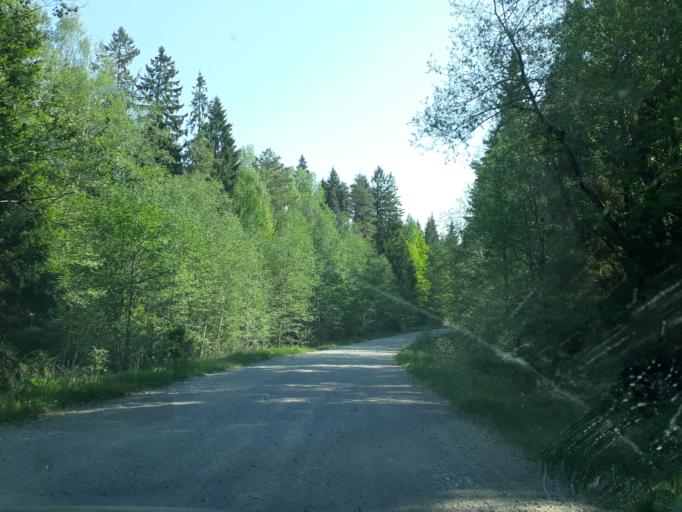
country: LV
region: Ligatne
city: Ligatne
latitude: 57.2799
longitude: 25.0780
